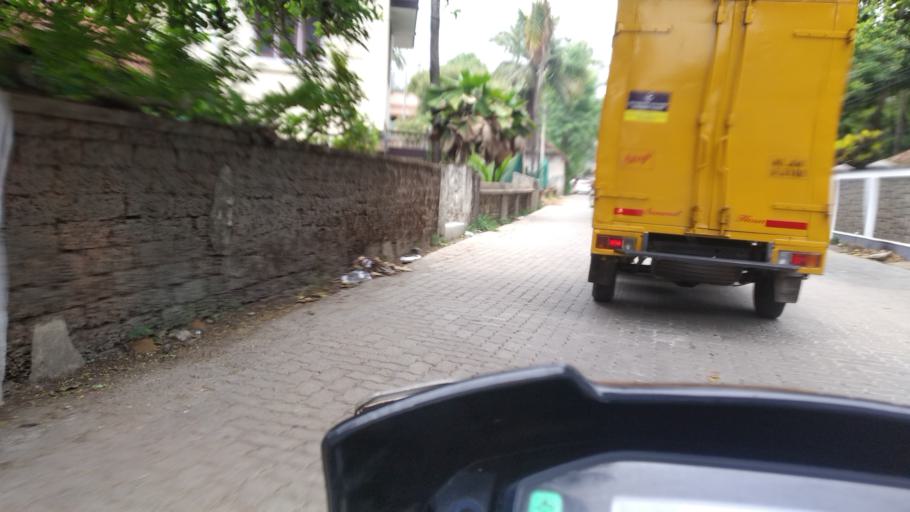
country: IN
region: Kerala
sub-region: Ernakulam
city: Perumpavur
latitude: 10.1179
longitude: 76.4774
